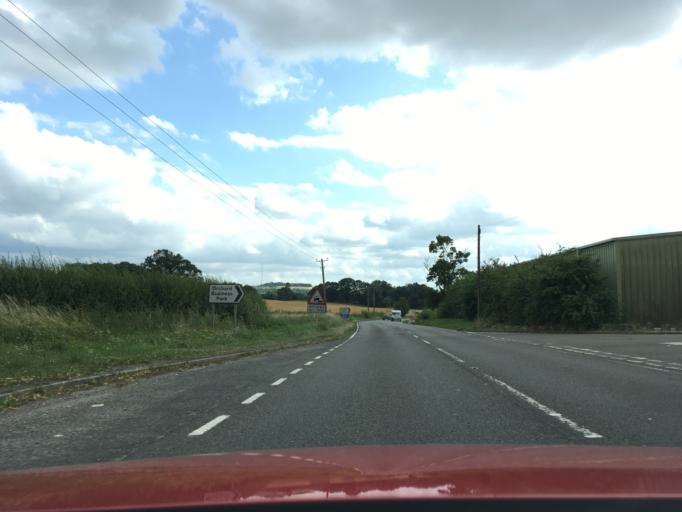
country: GB
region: England
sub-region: Hampshire
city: Kingsclere
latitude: 51.3405
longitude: -1.2585
